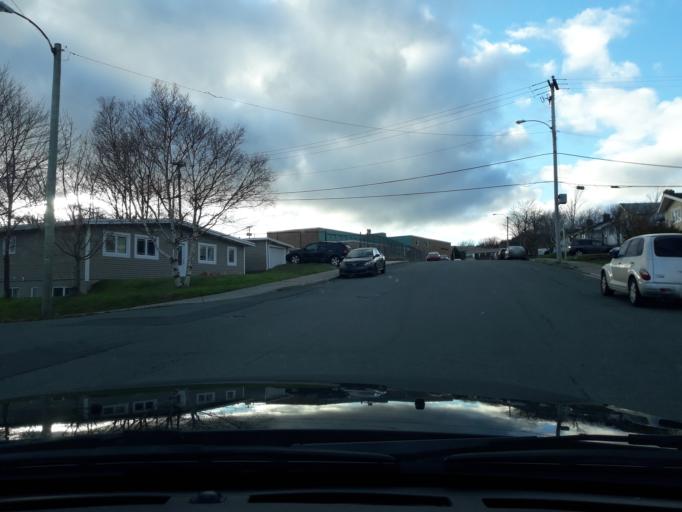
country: CA
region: Newfoundland and Labrador
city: St. John's
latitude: 47.5641
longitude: -52.7519
